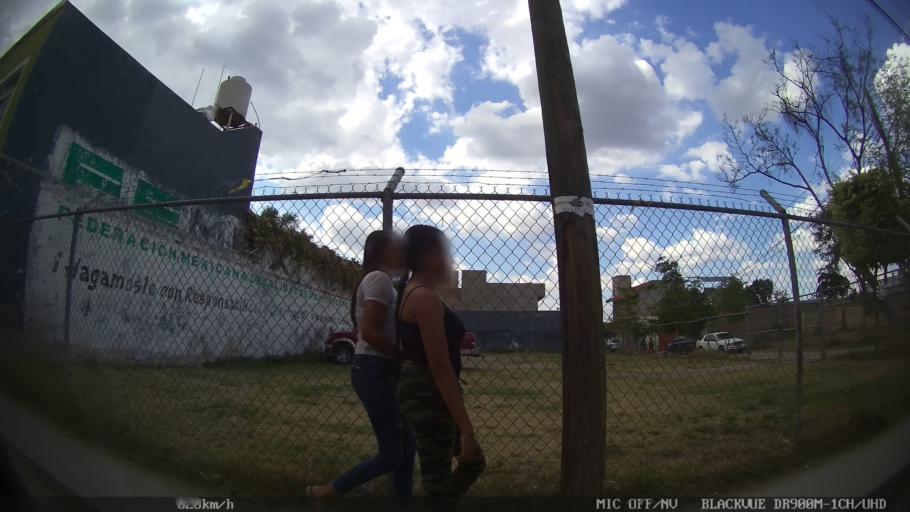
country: MX
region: Jalisco
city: Tlaquepaque
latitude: 20.6588
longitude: -103.2589
